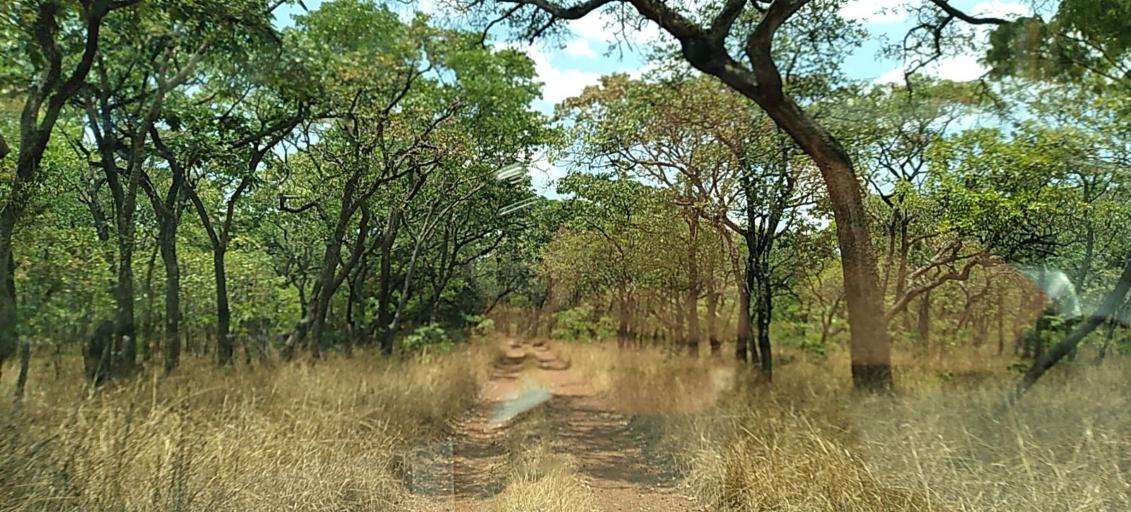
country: ZM
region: Copperbelt
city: Chililabombwe
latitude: -12.4515
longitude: 27.6971
